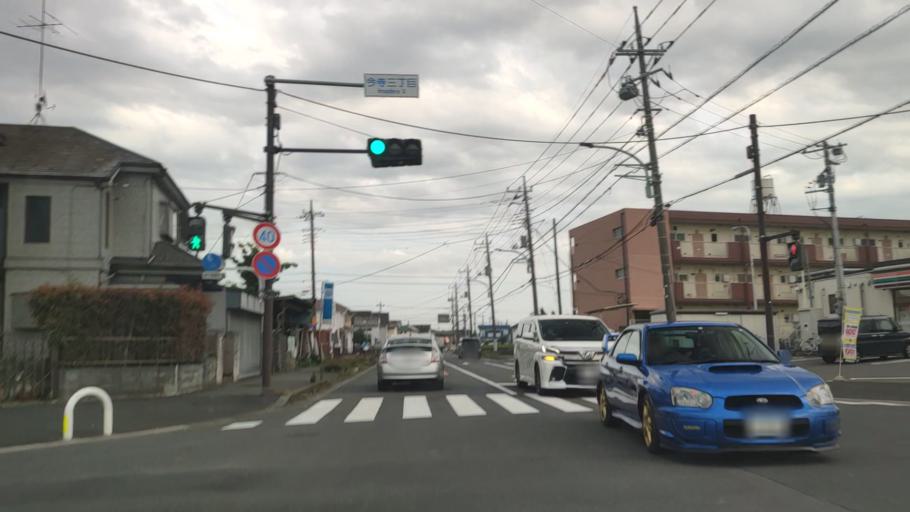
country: JP
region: Tokyo
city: Ome
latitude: 35.7966
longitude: 139.2981
